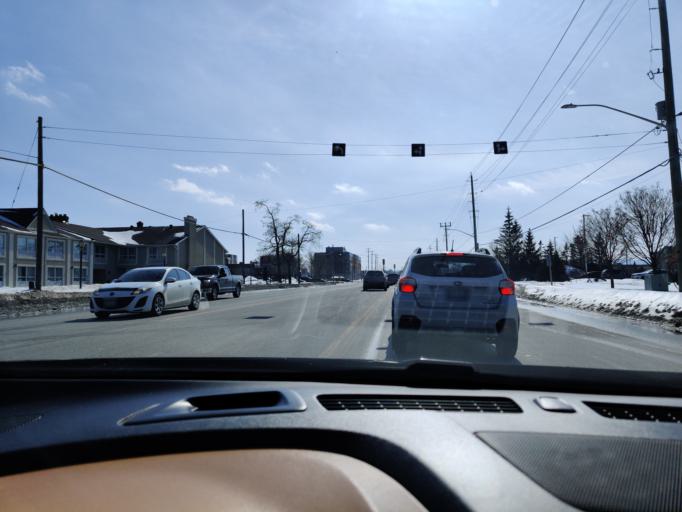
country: CA
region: Ontario
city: Collingwood
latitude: 44.5026
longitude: -80.2349
